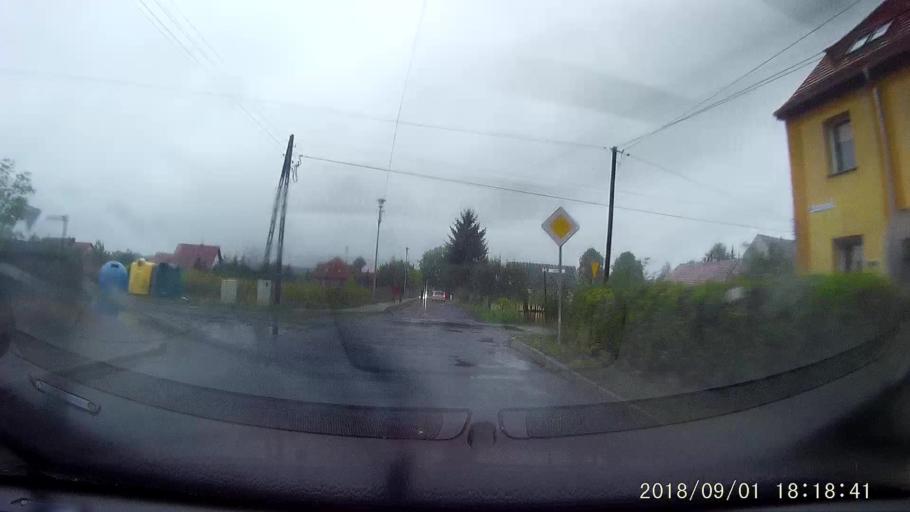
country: PL
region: Lower Silesian Voivodeship
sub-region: Powiat zgorzelecki
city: Piensk
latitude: 51.2584
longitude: 15.0457
